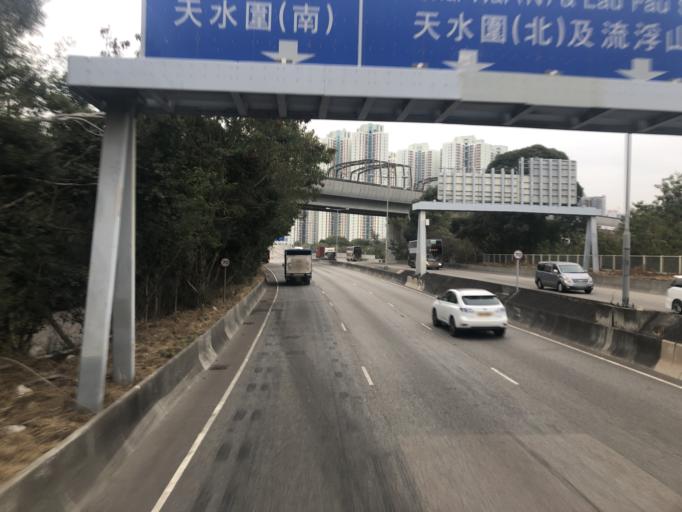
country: HK
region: Yuen Long
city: Yuen Long Kau Hui
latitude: 22.4429
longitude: 113.9990
